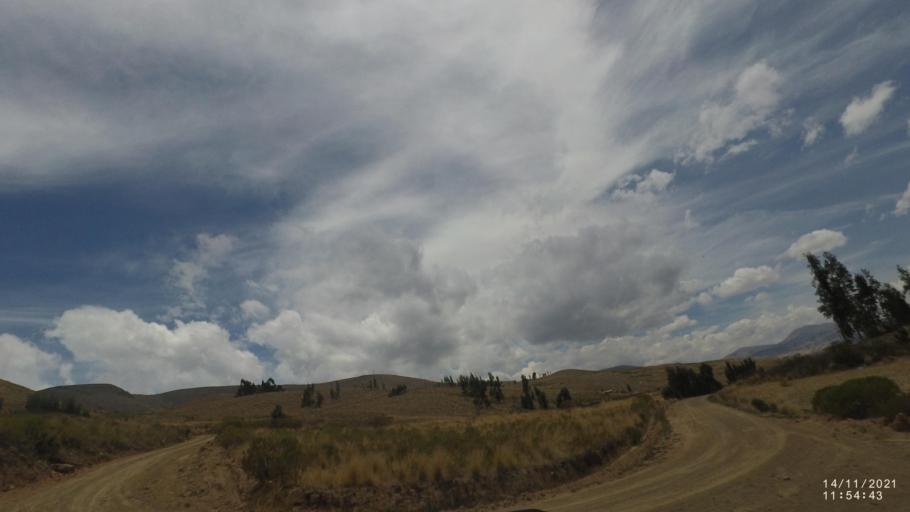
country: BO
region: Cochabamba
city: Colomi
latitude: -17.3620
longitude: -65.9795
